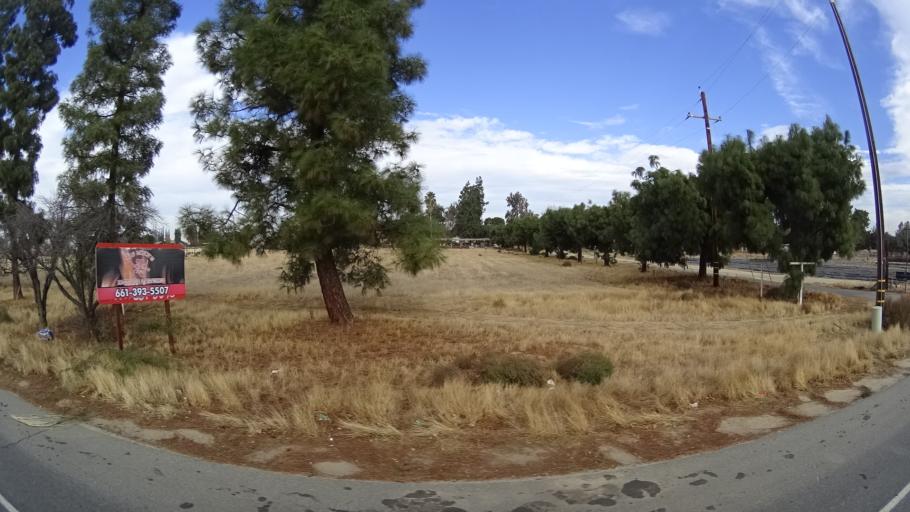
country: US
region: California
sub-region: Kern County
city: Rosedale
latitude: 35.4270
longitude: -119.1329
